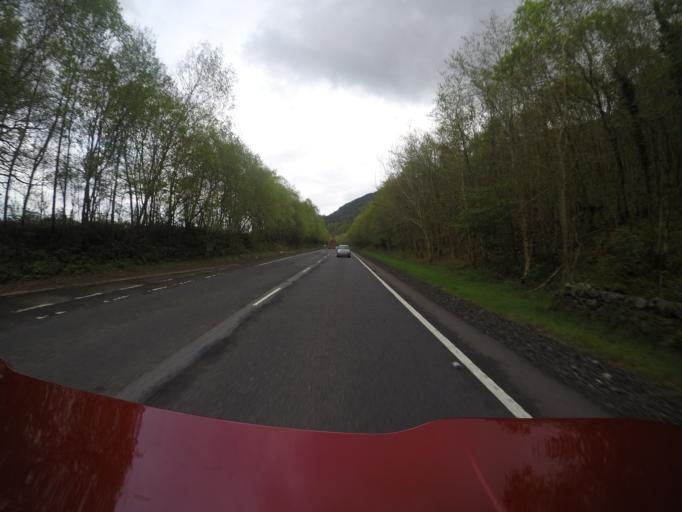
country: GB
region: Scotland
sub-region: Argyll and Bute
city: Helensburgh
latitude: 56.1236
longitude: -4.6525
